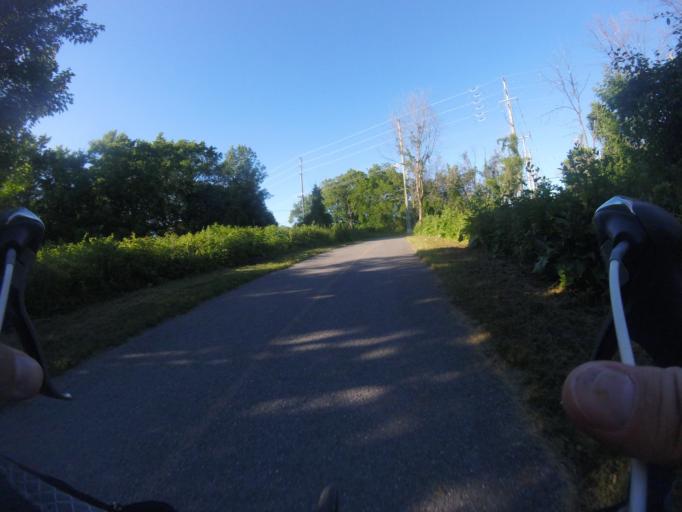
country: CA
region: Ontario
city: Bells Corners
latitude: 45.3355
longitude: -75.8107
